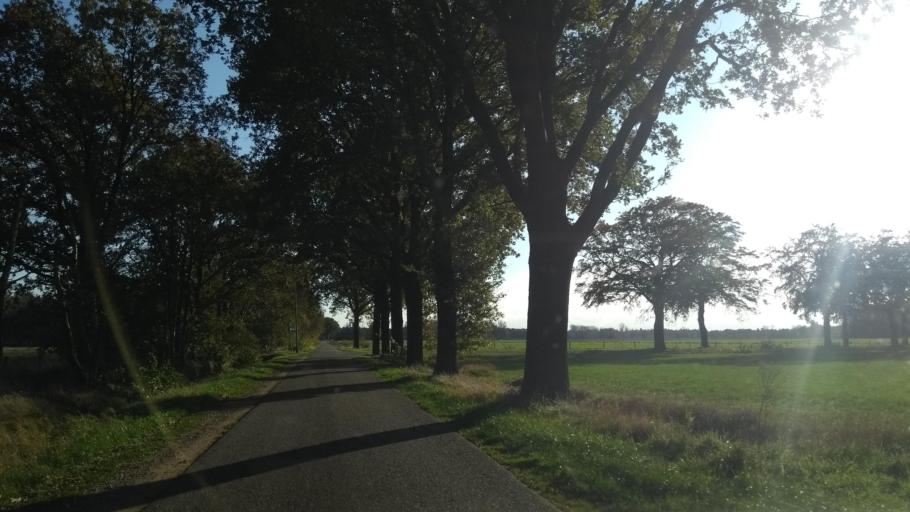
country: NL
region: Limburg
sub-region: Gemeente Leudal
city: Heythuysen
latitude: 51.3071
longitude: 5.8802
